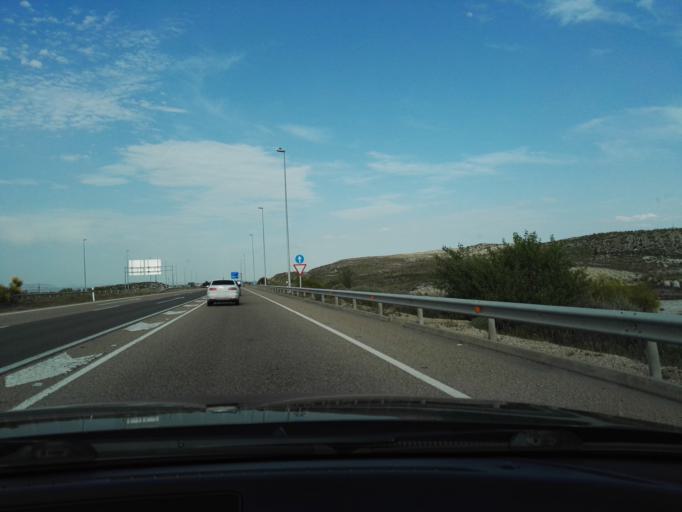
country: ES
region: Aragon
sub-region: Provincia de Zaragoza
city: Montecanal
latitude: 41.6187
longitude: -0.9571
